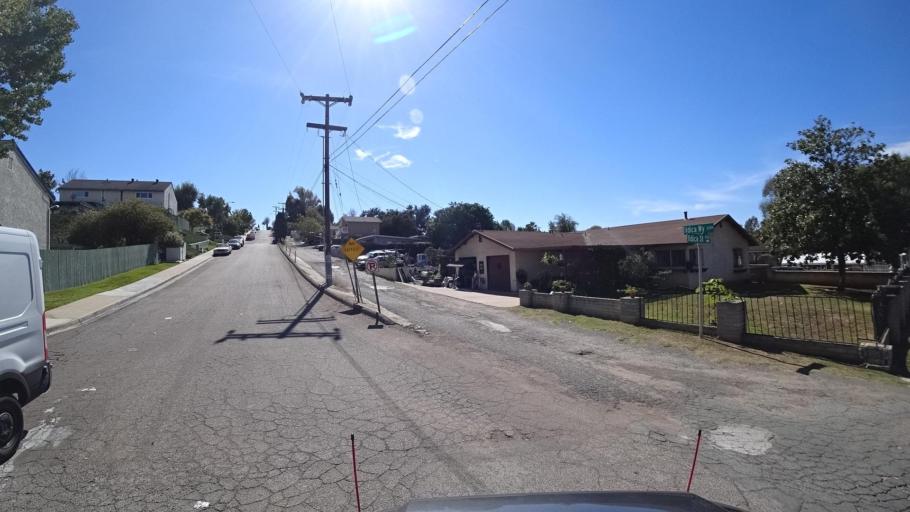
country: US
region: California
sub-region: San Diego County
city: Spring Valley
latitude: 32.7276
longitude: -117.0114
